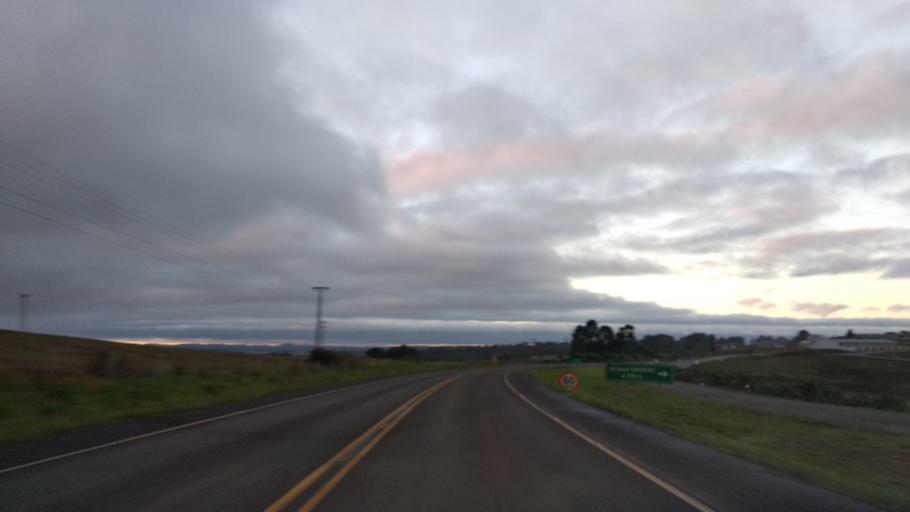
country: BR
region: Santa Catarina
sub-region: Campos Novos
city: Campos Novos
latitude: -27.3716
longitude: -51.2032
